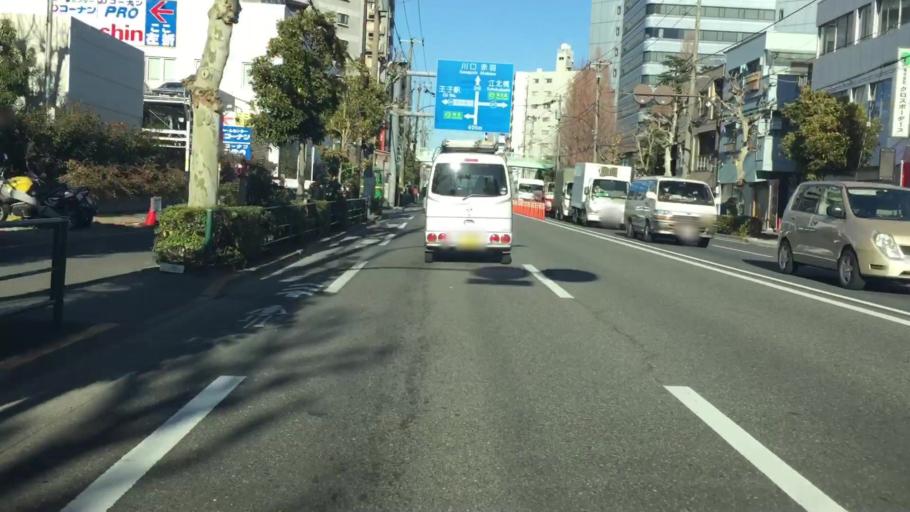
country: JP
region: Saitama
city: Kawaguchi
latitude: 35.7526
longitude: 139.7458
